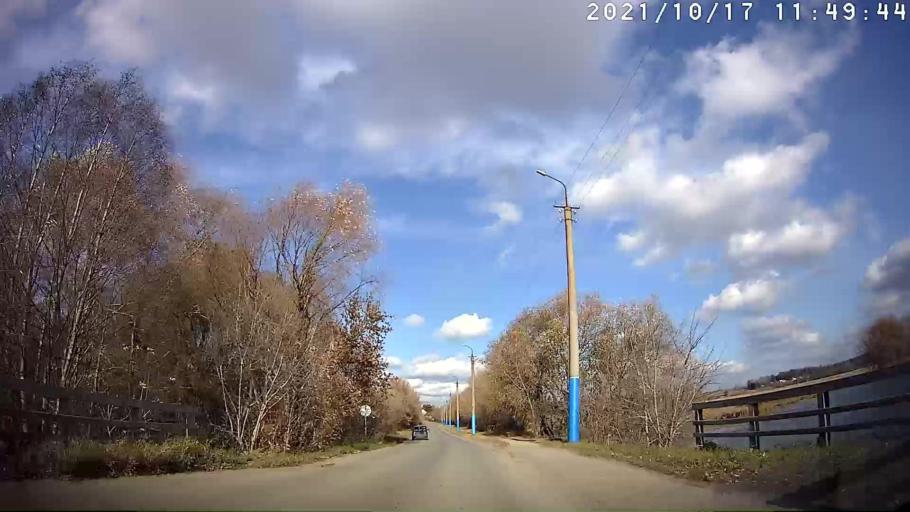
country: RU
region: Mariy-El
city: Kuzhener
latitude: 57.0079
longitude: 48.7368
